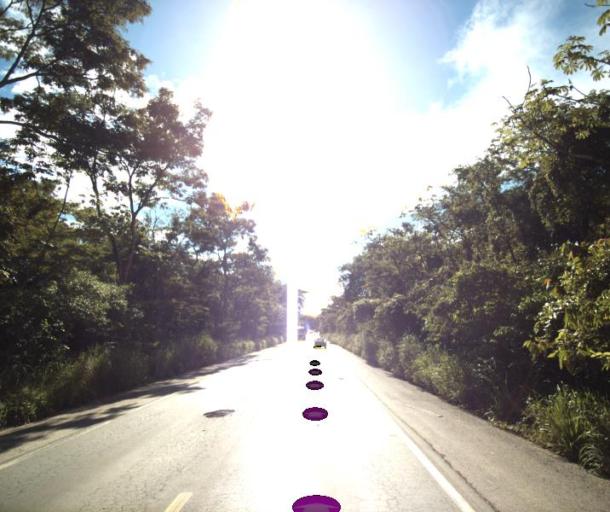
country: BR
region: Goias
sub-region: Uruana
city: Uruana
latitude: -15.5268
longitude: -49.4602
